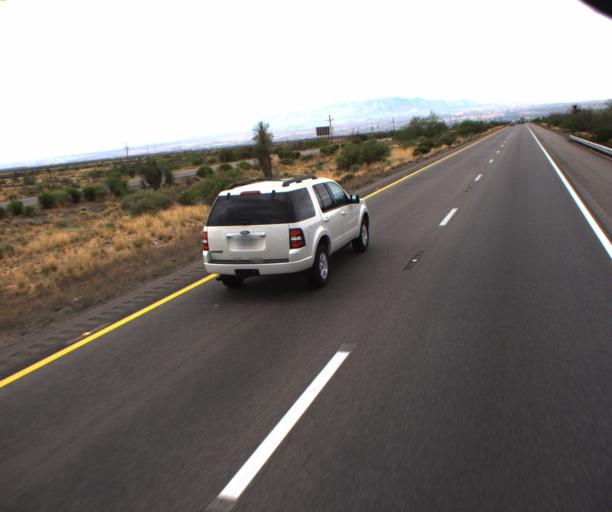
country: US
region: Arizona
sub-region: Cochise County
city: Saint David
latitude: 31.9896
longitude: -110.1849
